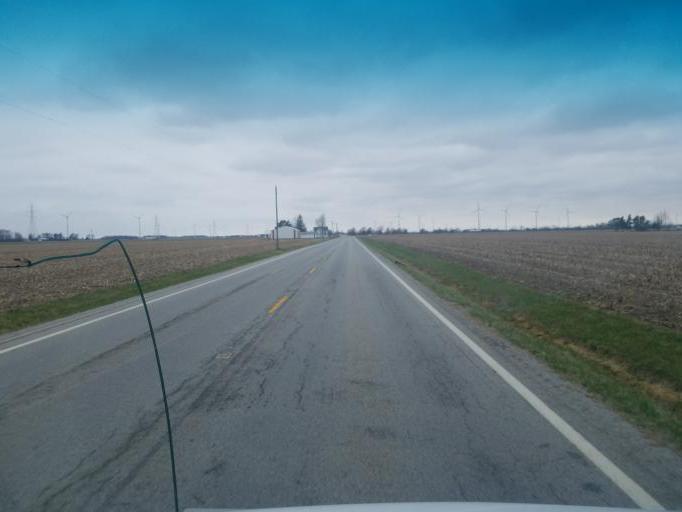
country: US
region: Ohio
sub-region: Van Wert County
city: Van Wert
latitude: 40.9320
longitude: -84.4905
